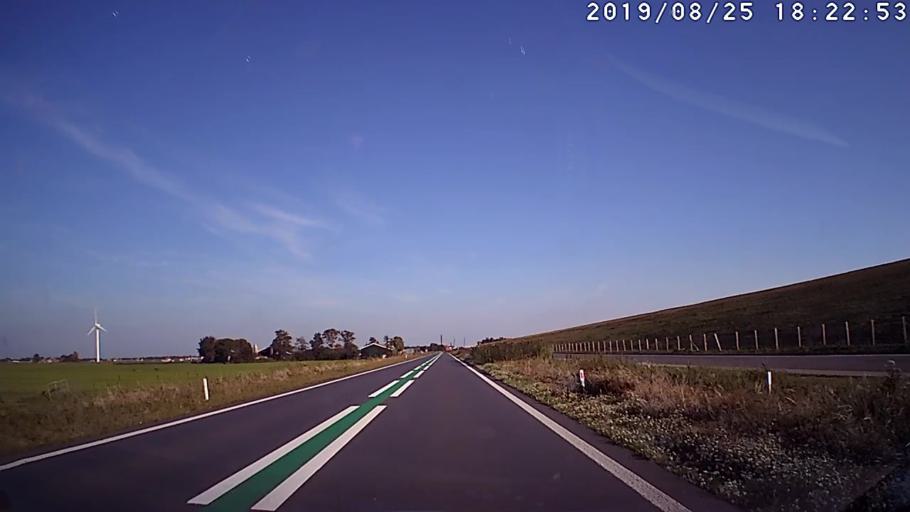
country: NL
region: Friesland
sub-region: Gemeente Lemsterland
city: Lemmer
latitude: 52.8611
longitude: 5.6556
